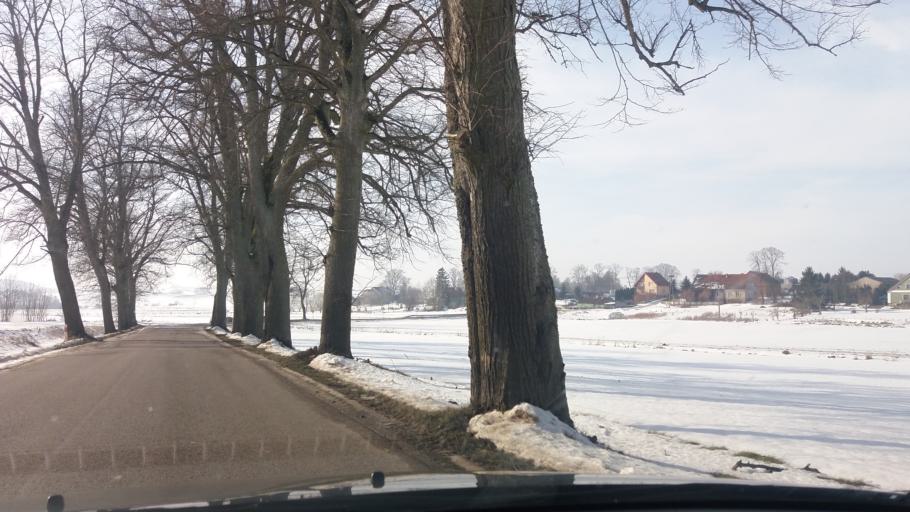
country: PL
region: Warmian-Masurian Voivodeship
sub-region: Powiat bartoszycki
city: Bisztynek
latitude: 54.1019
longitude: 20.8080
